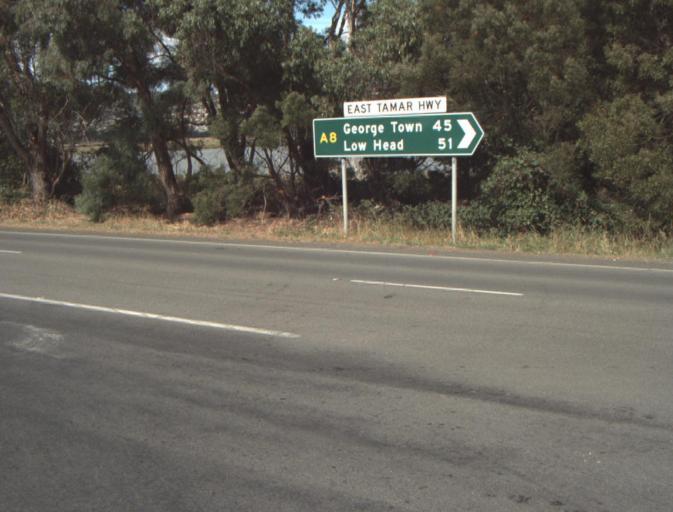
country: AU
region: Tasmania
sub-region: Launceston
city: Newnham
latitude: -41.3985
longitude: 147.1158
